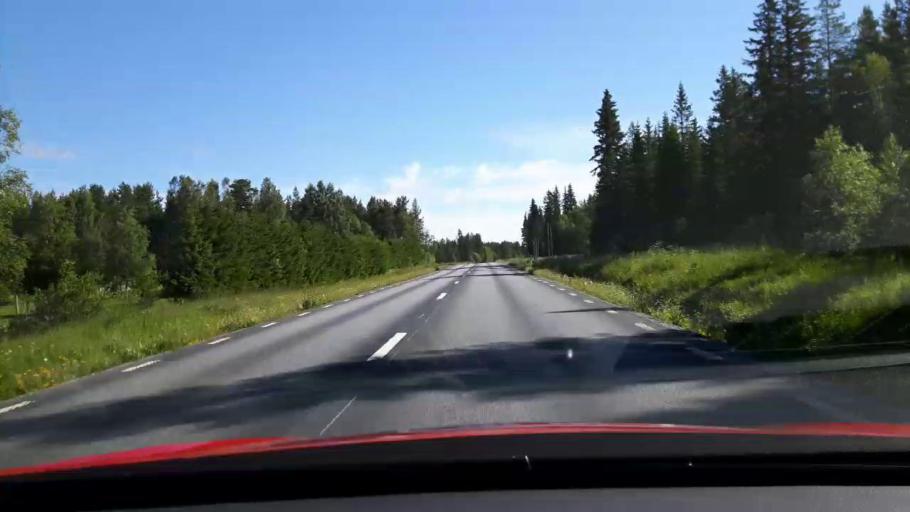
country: SE
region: Jaemtland
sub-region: OEstersunds Kommun
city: Ostersund
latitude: 63.2240
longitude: 14.7437
